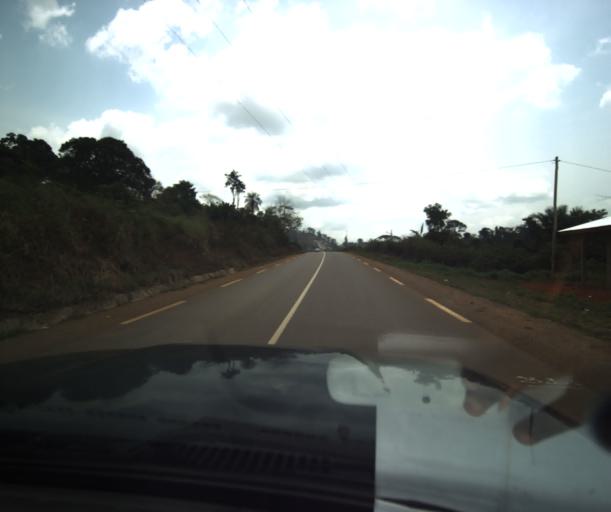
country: CM
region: Centre
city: Mbankomo
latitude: 3.7862
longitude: 11.4172
